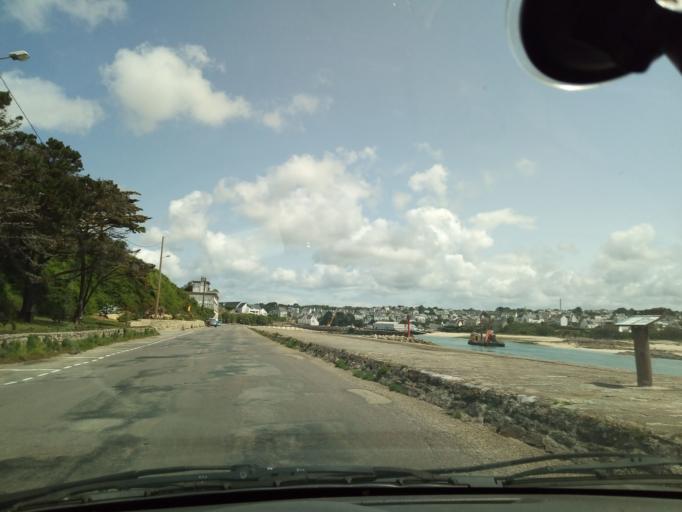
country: FR
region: Brittany
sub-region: Departement du Finistere
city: Audierne
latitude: 48.0140
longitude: -4.5399
